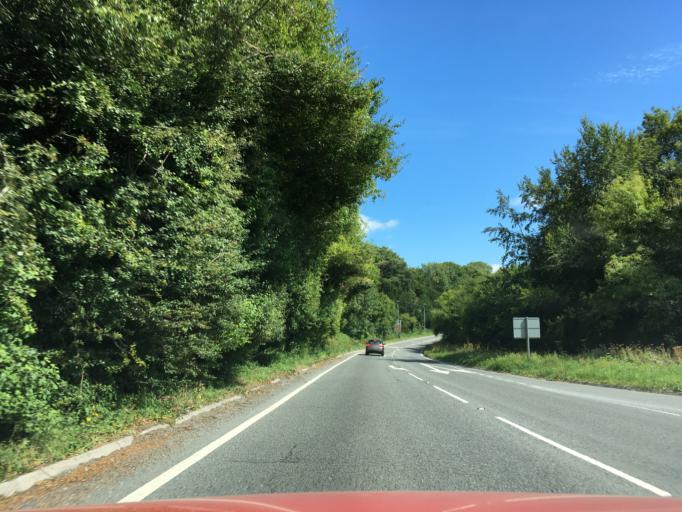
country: GB
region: England
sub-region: Dorset
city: Dorchester
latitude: 50.7503
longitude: -2.5141
